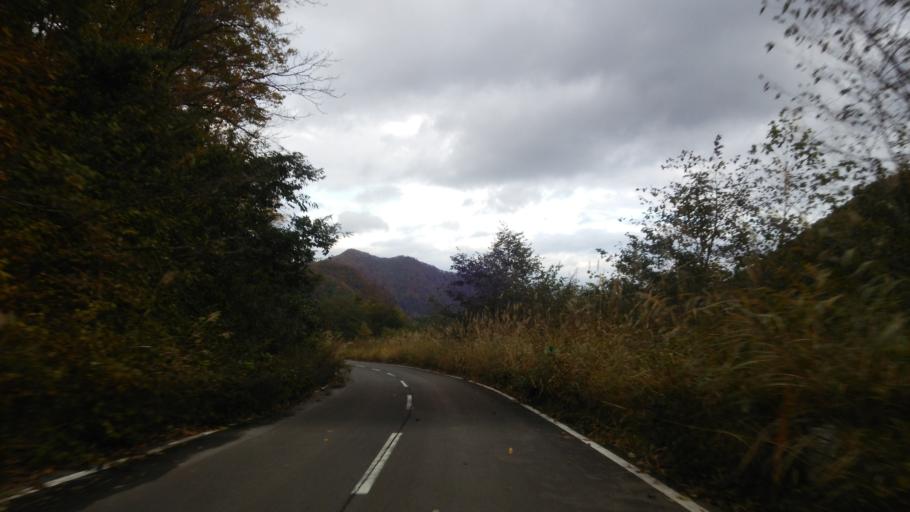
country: JP
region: Fukushima
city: Kitakata
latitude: 37.3798
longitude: 139.7083
